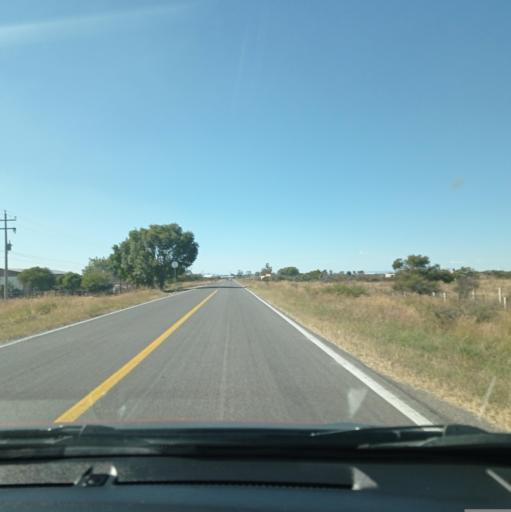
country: MX
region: Jalisco
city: Valle de Guadalupe
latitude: 21.0210
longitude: -102.5341
